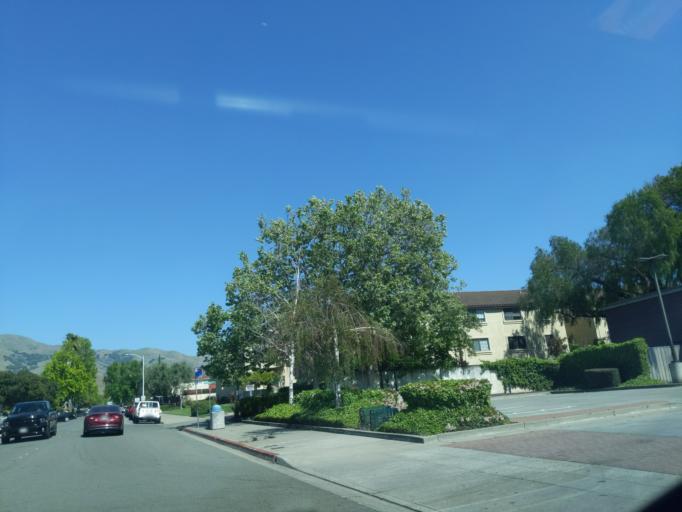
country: US
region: California
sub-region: Santa Clara County
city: Milpitas
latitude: 37.4525
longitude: -121.9102
